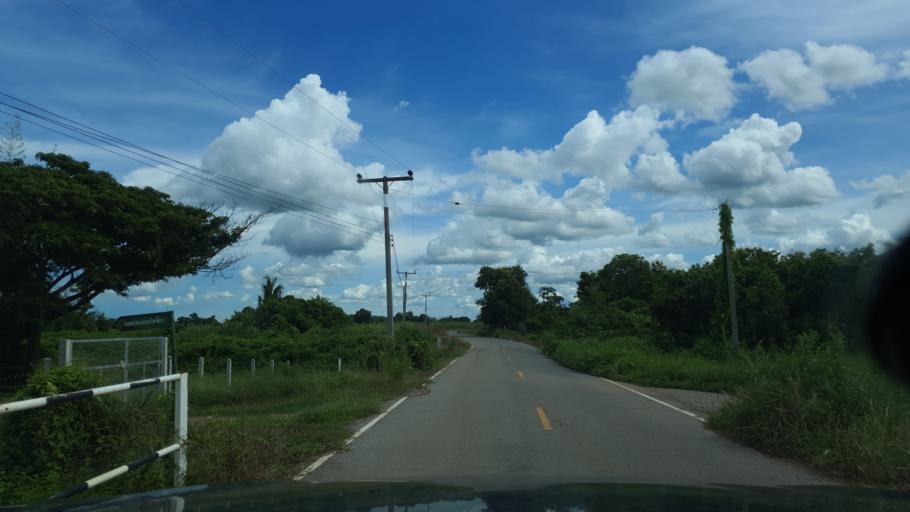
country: TH
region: Sukhothai
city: Thung Saliam
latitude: 17.3497
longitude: 99.6405
